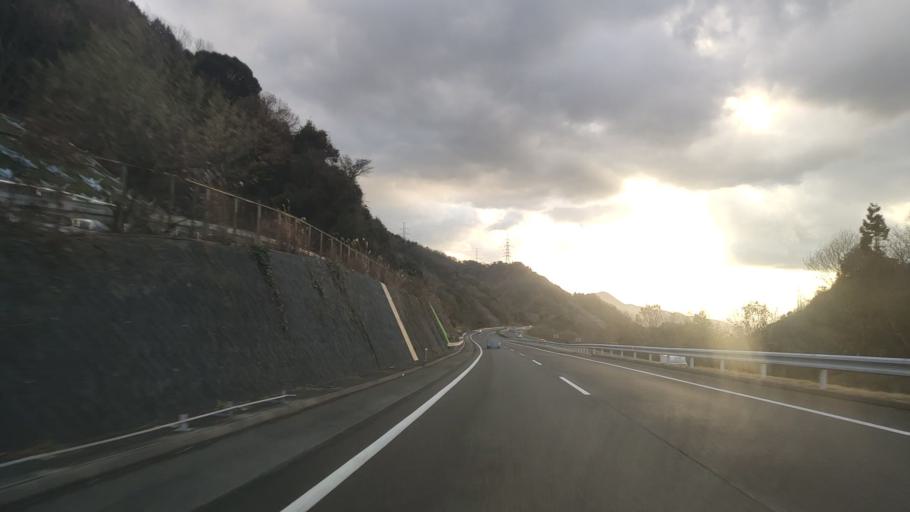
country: JP
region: Ehime
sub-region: Shikoku-chuo Shi
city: Matsuyama
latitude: 33.8163
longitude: 132.9579
